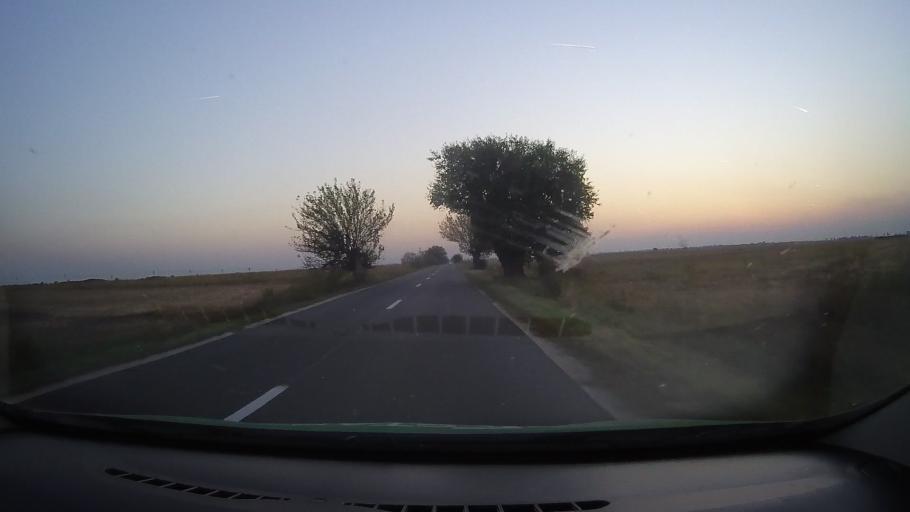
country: RO
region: Arad
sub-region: Comuna Zimandu Nou
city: Zimandu Nou
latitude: 46.2957
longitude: 21.4217
